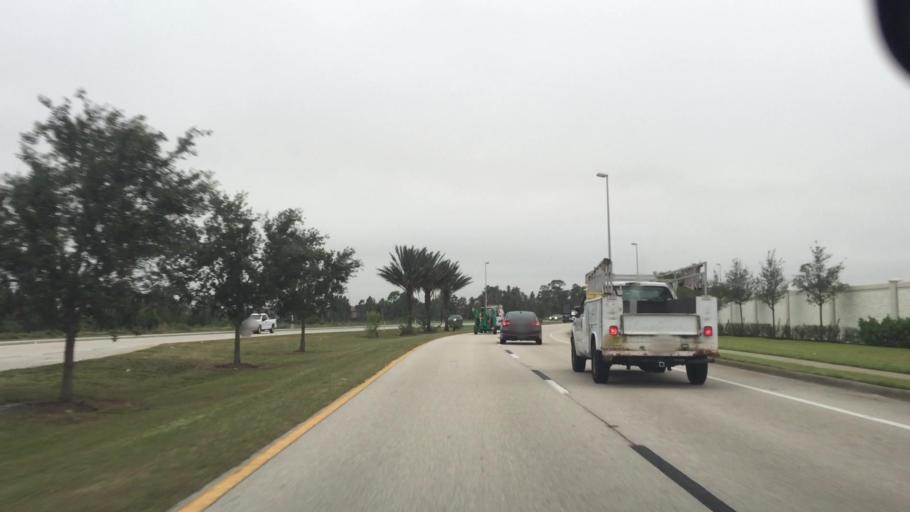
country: US
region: Florida
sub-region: Lee County
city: Three Oaks
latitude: 26.4887
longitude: -81.7997
